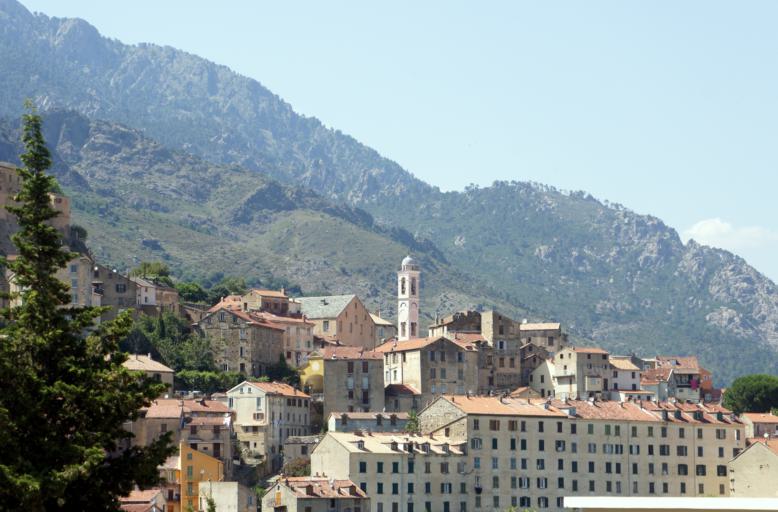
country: FR
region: Corsica
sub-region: Departement de la Haute-Corse
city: Corte
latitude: 42.3032
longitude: 9.1502
